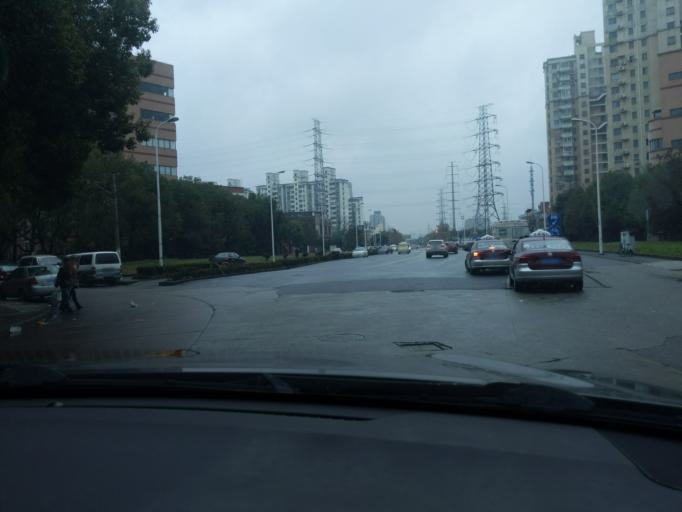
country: CN
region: Shanghai Shi
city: Huamu
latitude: 31.1887
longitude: 121.5250
